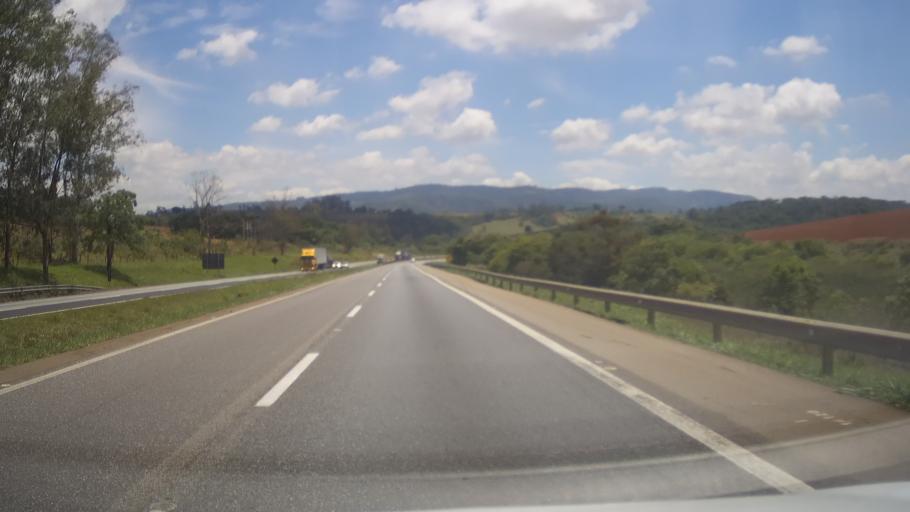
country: BR
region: Minas Gerais
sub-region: Sao Goncalo Do Sapucai
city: Sao Goncalo do Sapucai
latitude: -21.9267
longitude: -45.6116
